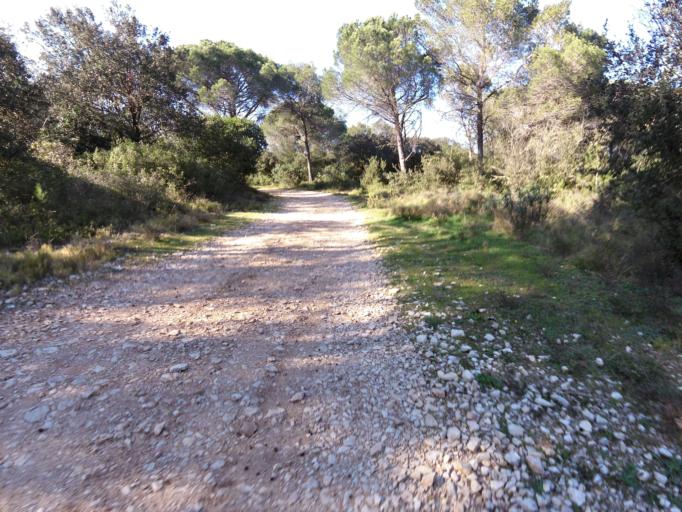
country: FR
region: Languedoc-Roussillon
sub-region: Departement du Gard
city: Congenies
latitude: 43.7610
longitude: 4.1682
